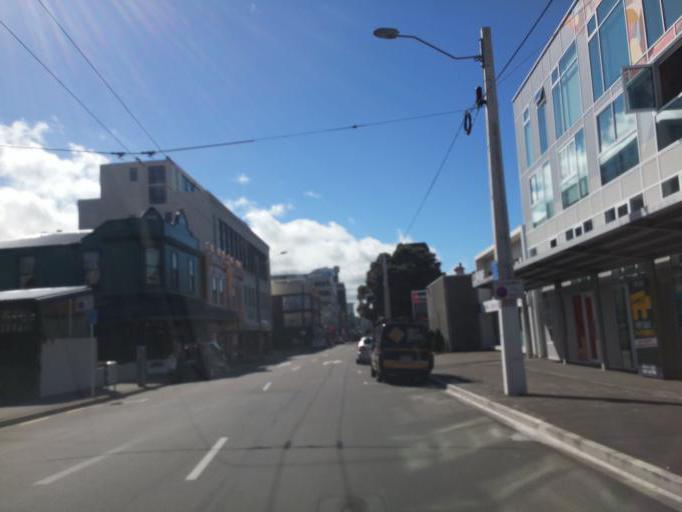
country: NZ
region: Wellington
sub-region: Wellington City
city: Wellington
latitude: -41.2953
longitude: 174.7712
